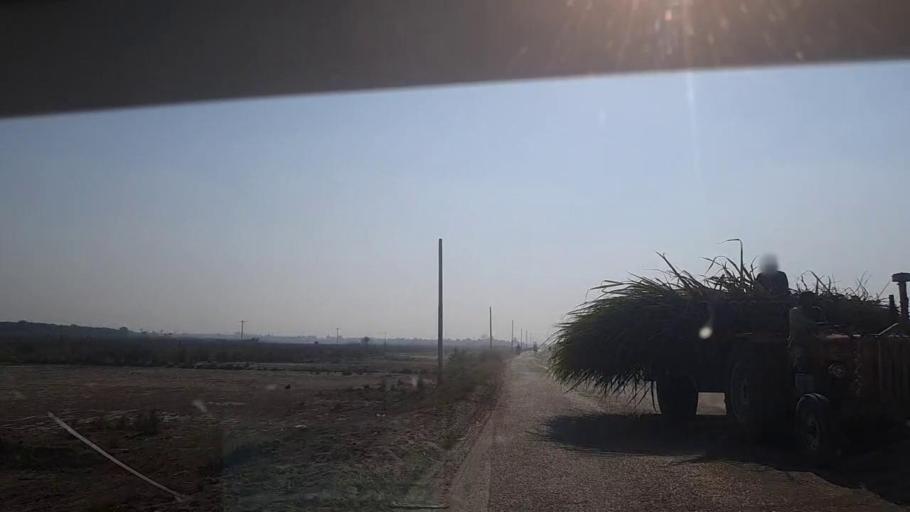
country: PK
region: Sindh
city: Gambat
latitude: 27.3600
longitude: 68.5546
